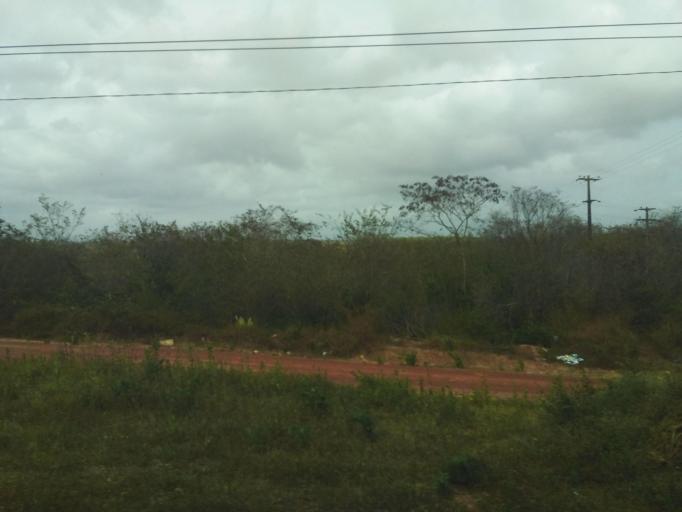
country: BR
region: Maranhao
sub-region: Icatu
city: Icatu
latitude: -2.9170
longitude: -44.3535
